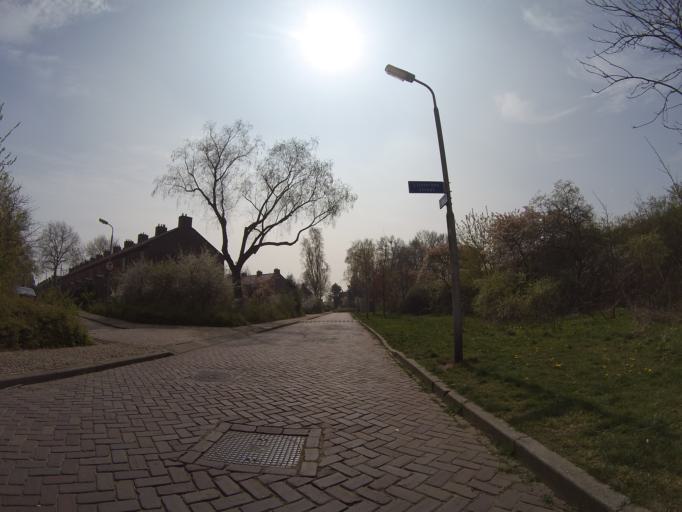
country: NL
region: Utrecht
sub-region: Gemeente Amersfoort
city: Hoogland
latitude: 52.1605
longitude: 5.3502
